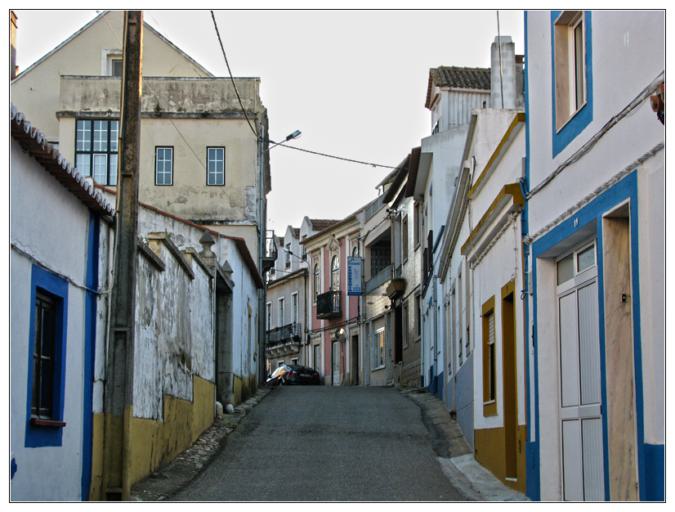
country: PT
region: Setubal
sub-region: Santiago do Cacem
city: Cercal
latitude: 37.8031
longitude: -8.6737
